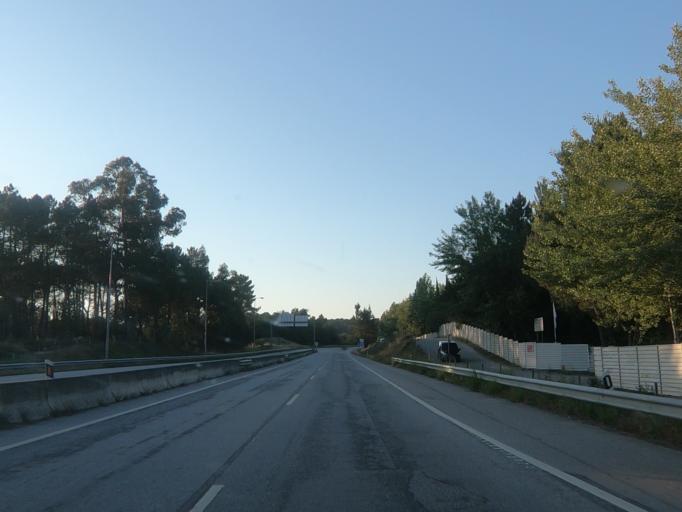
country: PT
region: Viseu
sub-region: Viseu
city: Rio de Loba
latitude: 40.6572
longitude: -7.8624
